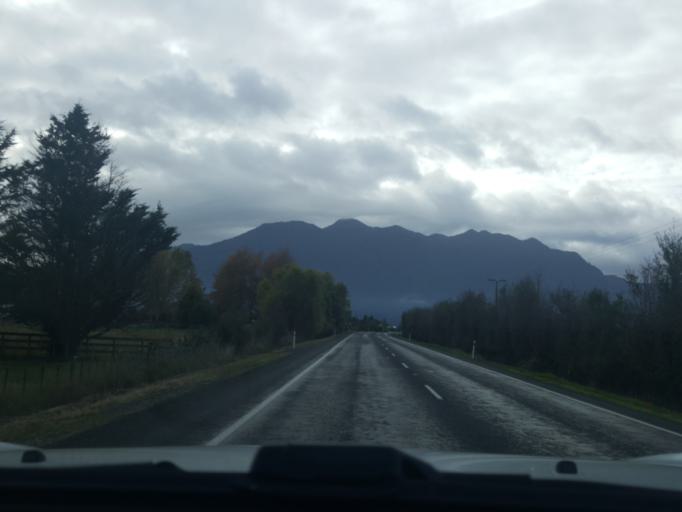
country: NZ
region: Waikato
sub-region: Hauraki District
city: Paeroa
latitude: -37.5610
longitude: 175.6859
